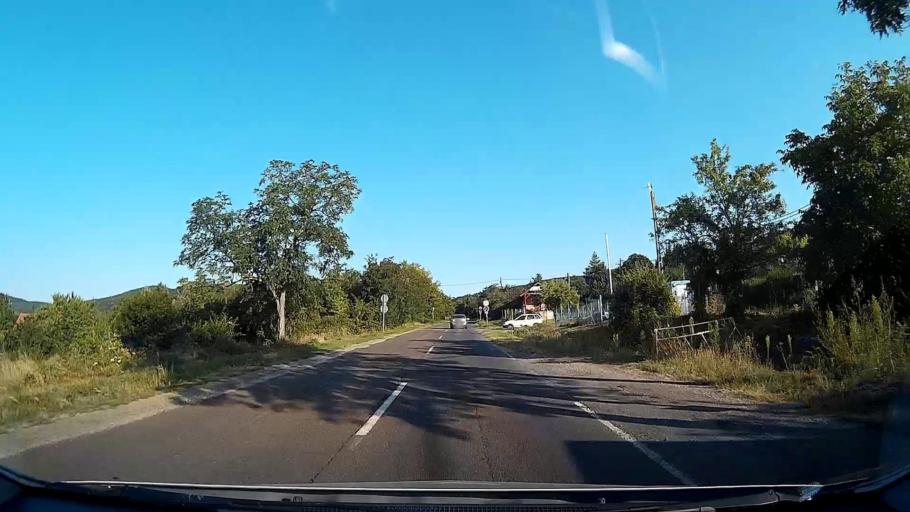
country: HU
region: Pest
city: Szentendre
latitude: 47.6991
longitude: 19.0357
